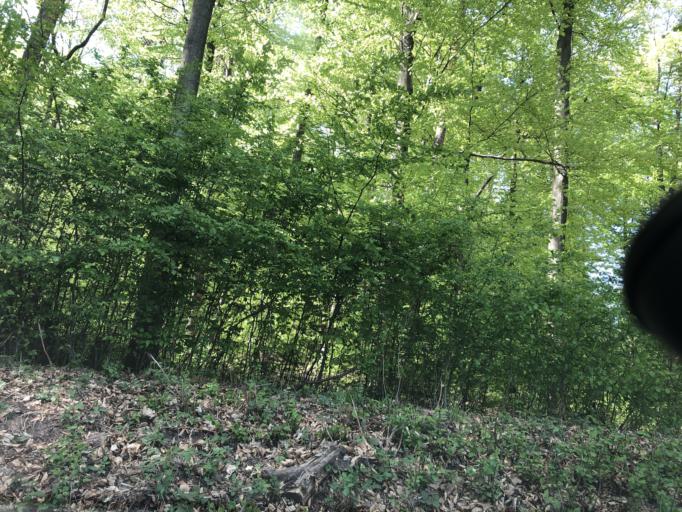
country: DE
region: Baden-Wuerttemberg
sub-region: Karlsruhe Region
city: Schonau
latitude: 49.4395
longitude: 8.8011
